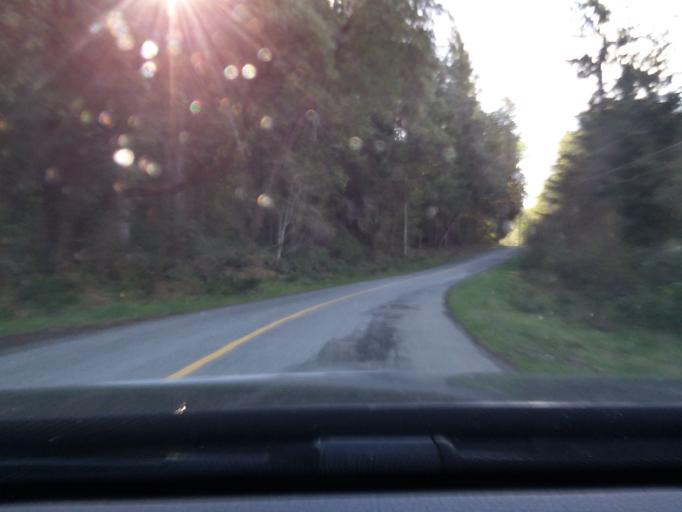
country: CA
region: British Columbia
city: North Cowichan
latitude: 48.9646
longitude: -123.5506
